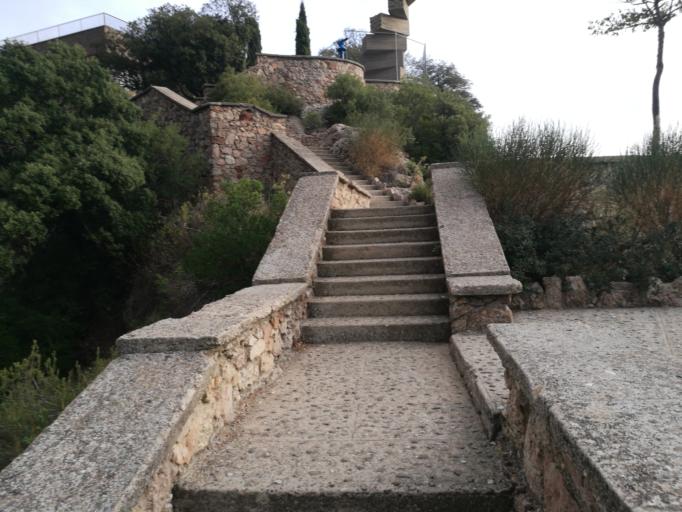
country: ES
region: Catalonia
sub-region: Provincia de Barcelona
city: Monistrol de Montserrat
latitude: 41.5938
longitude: 1.8412
